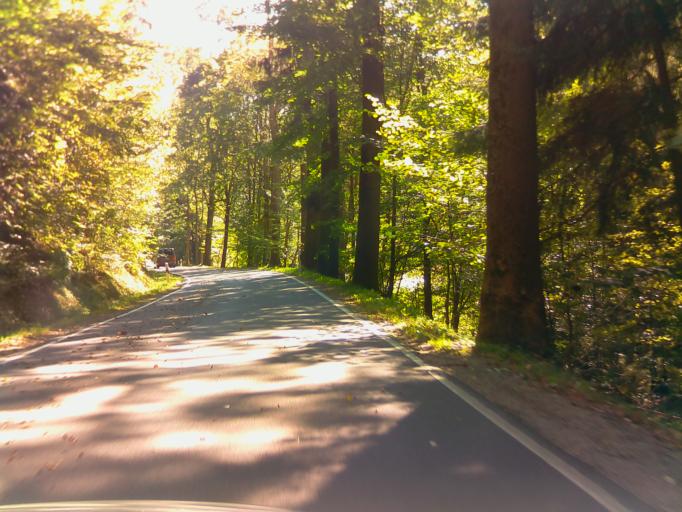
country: DE
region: Thuringia
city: Wurzbach
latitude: 50.5001
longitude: 11.4910
